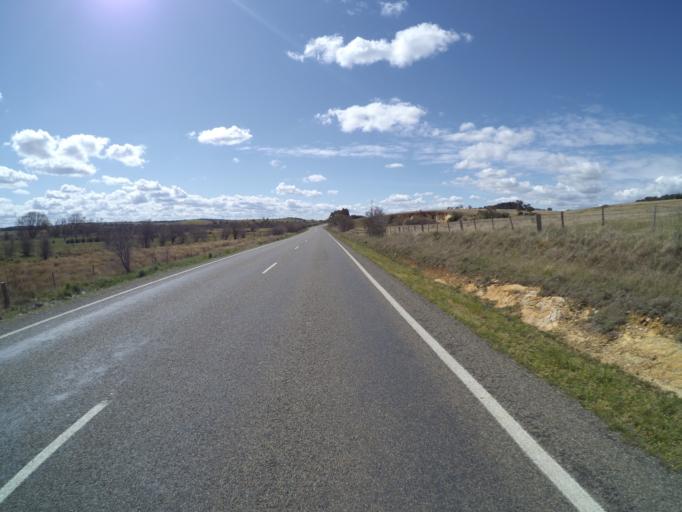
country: AU
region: New South Wales
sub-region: Goulburn Mulwaree
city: Goulburn
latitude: -34.8001
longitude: 149.6904
